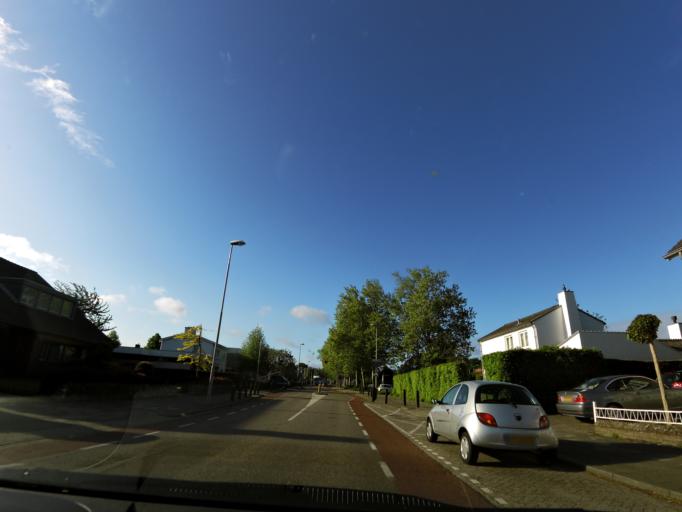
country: NL
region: Limburg
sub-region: Gemeente Voerendaal
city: Kunrade
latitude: 50.8798
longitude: 5.9314
